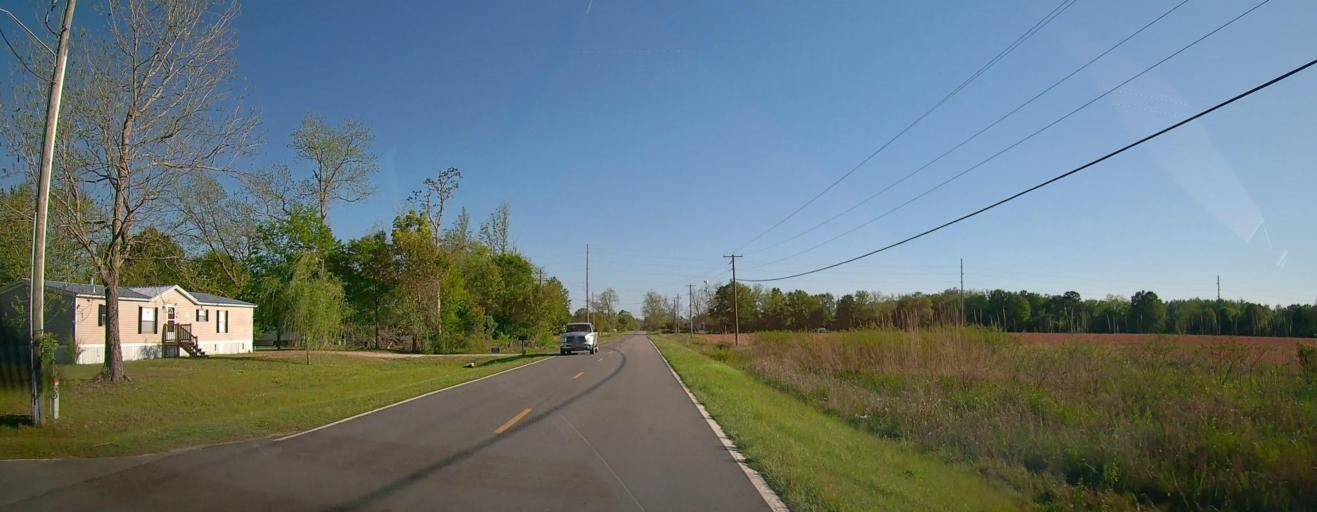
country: US
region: Georgia
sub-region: Ben Hill County
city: Fitzgerald
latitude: 31.7365
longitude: -83.2802
